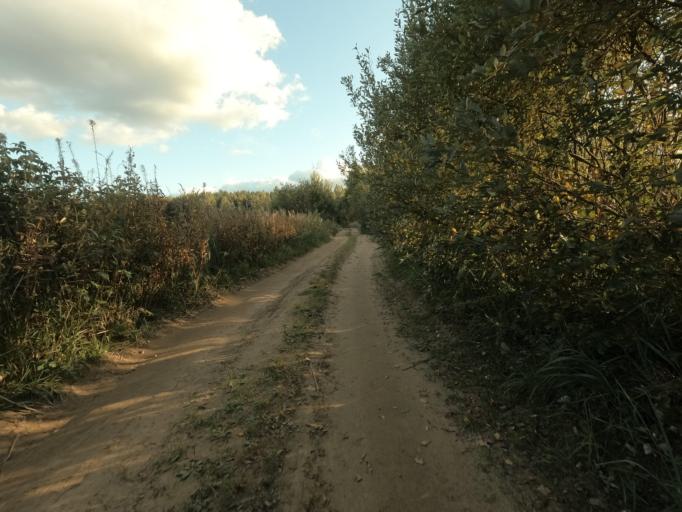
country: RU
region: Leningrad
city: Otradnoye
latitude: 59.8554
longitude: 30.7959
